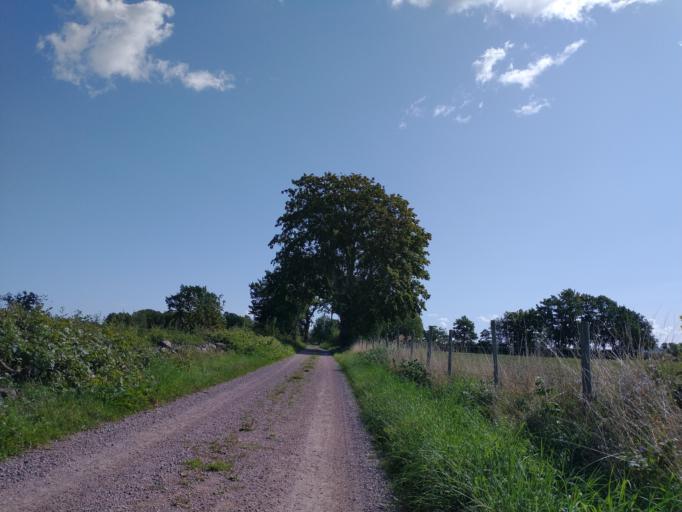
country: SE
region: Kalmar
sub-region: Kalmar Kommun
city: Lindsdal
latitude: 56.7919
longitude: 16.2946
